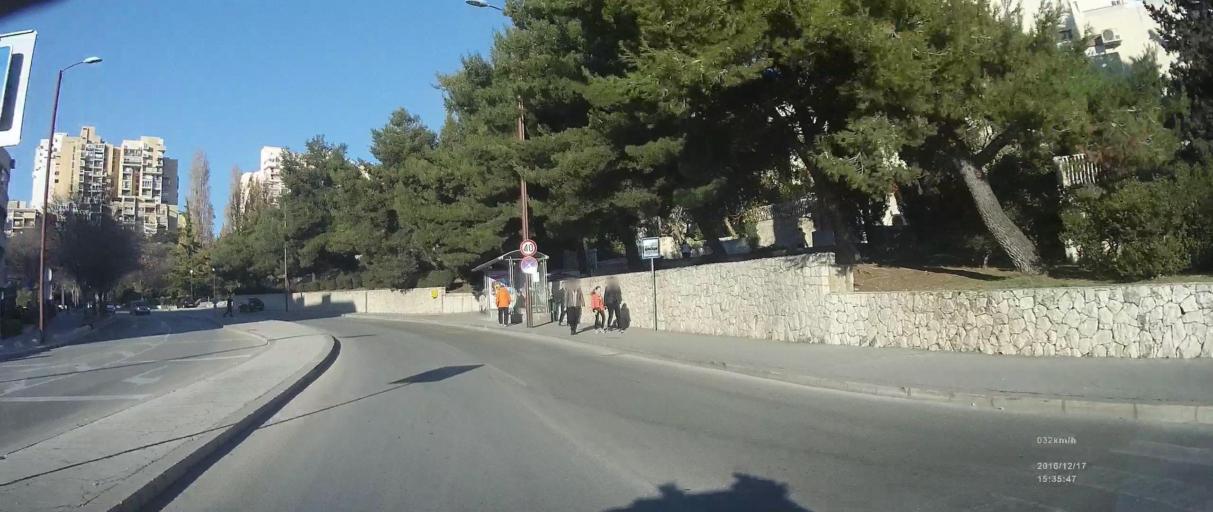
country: HR
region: Splitsko-Dalmatinska
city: Vranjic
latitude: 43.5061
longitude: 16.4789
